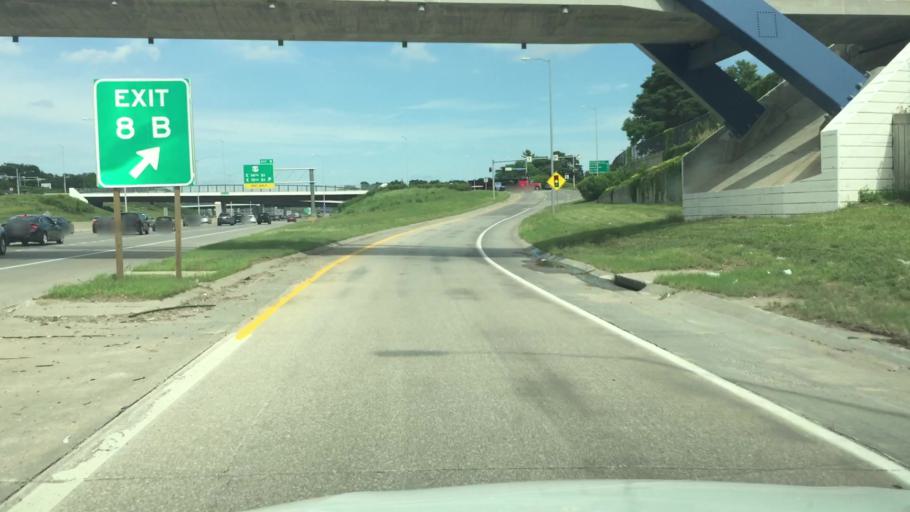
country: US
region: Iowa
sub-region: Polk County
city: Des Moines
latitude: 41.5951
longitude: -93.6135
